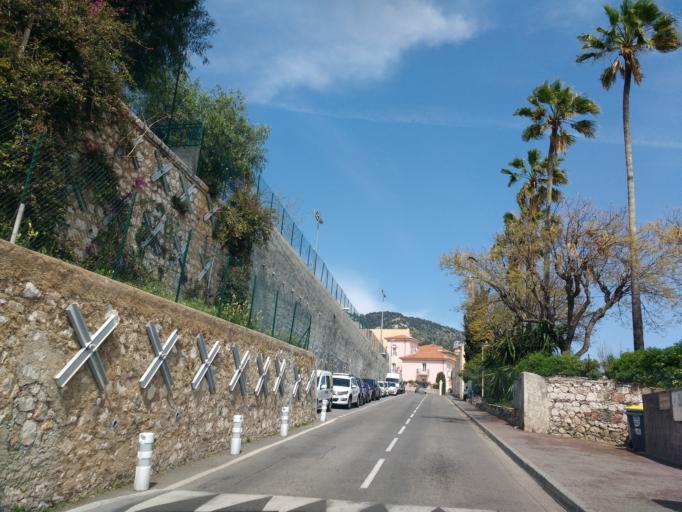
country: FR
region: Provence-Alpes-Cote d'Azur
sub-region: Departement des Alpes-Maritimes
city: Villefranche-sur-Mer
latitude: 43.7009
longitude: 7.3086
